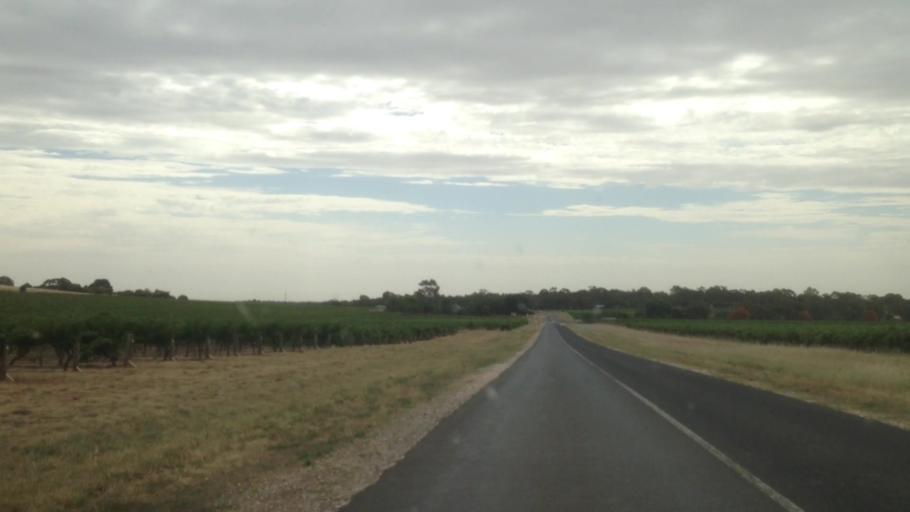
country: AU
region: South Australia
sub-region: Barossa
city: Lyndoch
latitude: -34.5983
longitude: 138.9249
